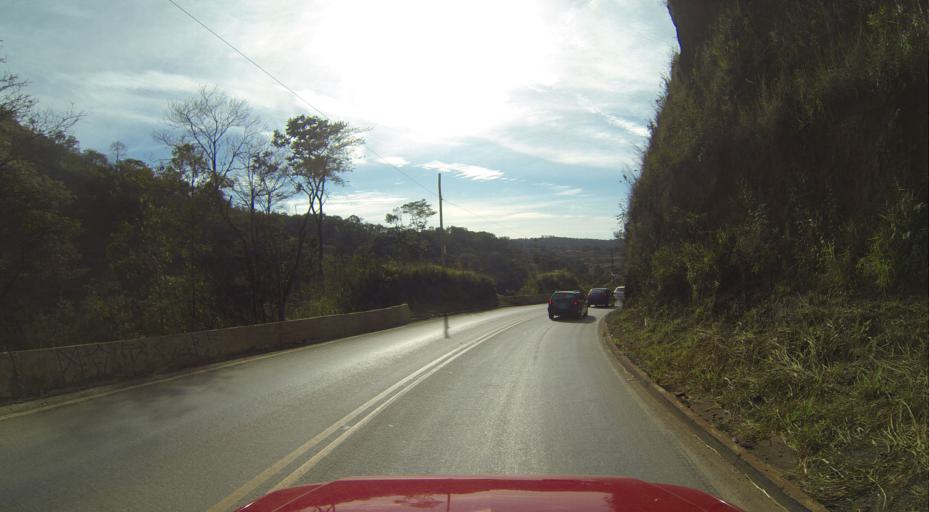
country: BR
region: Minas Gerais
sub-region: Brumadinho
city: Brumadinho
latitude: -20.1009
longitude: -44.2095
